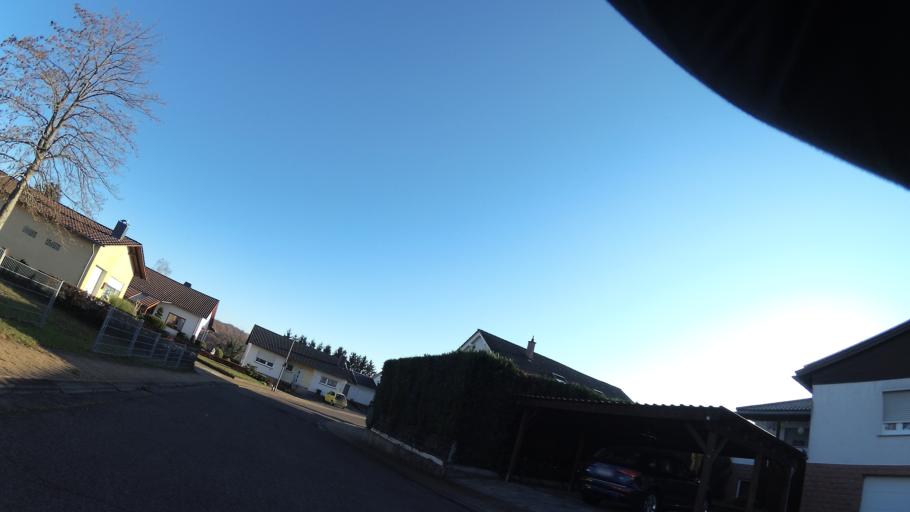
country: DE
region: Saarland
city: Schwalbach
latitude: 49.2994
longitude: 6.8426
